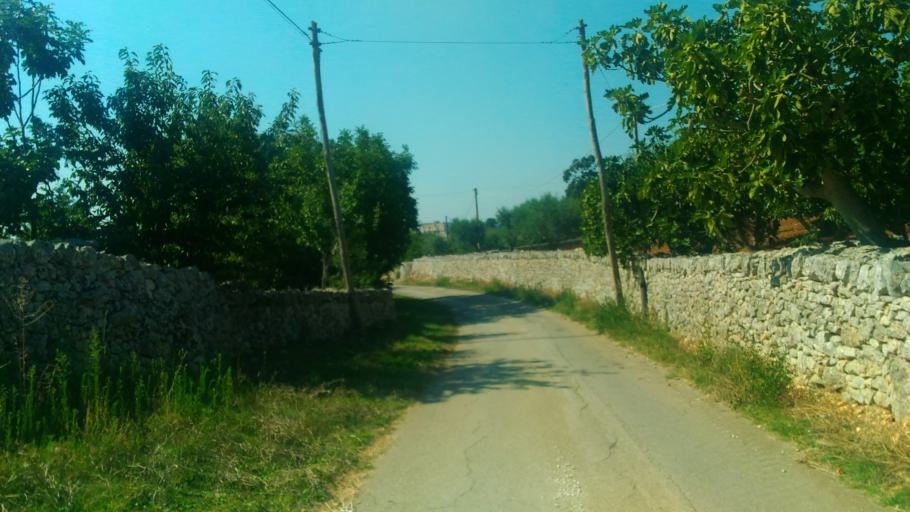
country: IT
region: Apulia
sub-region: Provincia di Bari
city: Noci
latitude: 40.8198
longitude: 17.1755
